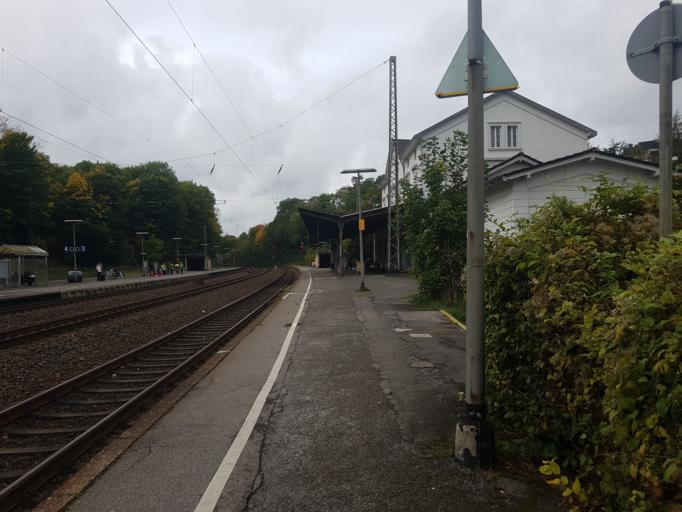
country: DE
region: North Rhine-Westphalia
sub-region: Regierungsbezirk Koln
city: Eschweiler
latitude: 50.8134
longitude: 6.2527
